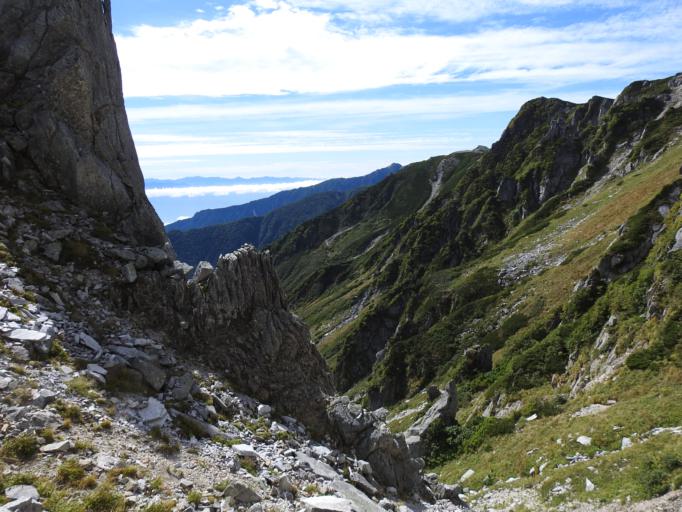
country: JP
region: Nagano
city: Ina
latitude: 35.7829
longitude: 137.8108
